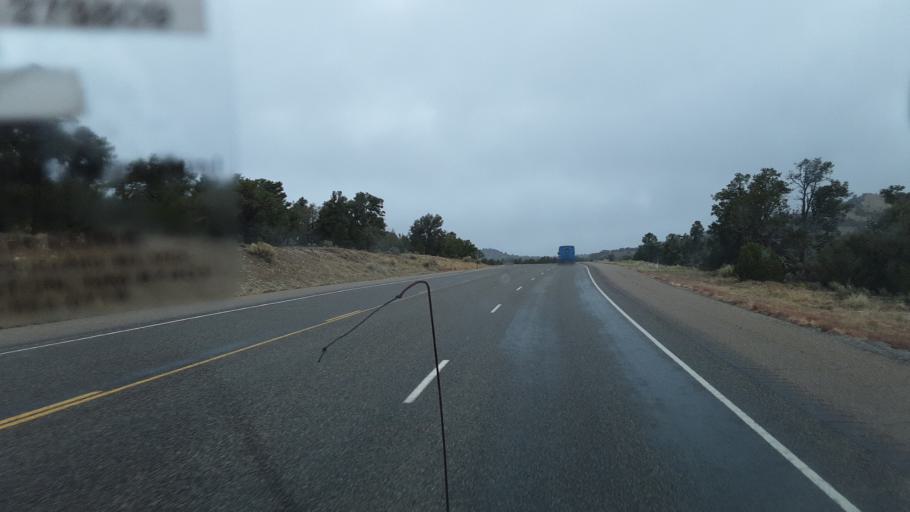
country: US
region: New Mexico
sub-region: Rio Arriba County
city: Tierra Amarilla
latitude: 36.4526
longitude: -106.4767
